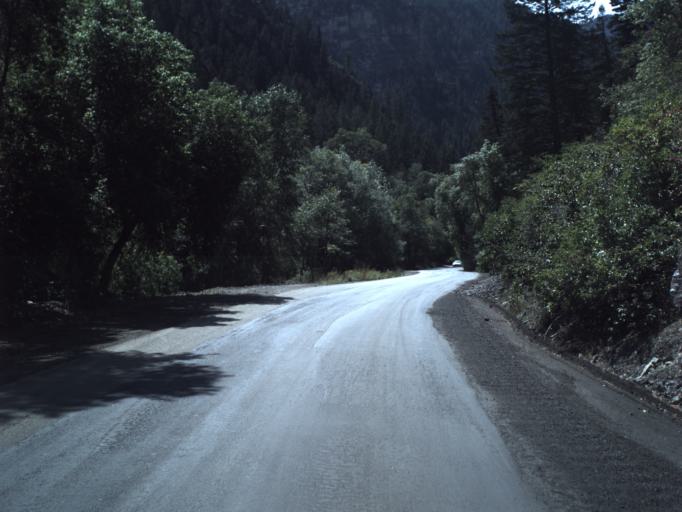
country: US
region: Utah
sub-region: Utah County
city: Cedar Hills
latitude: 40.4581
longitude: -111.6588
